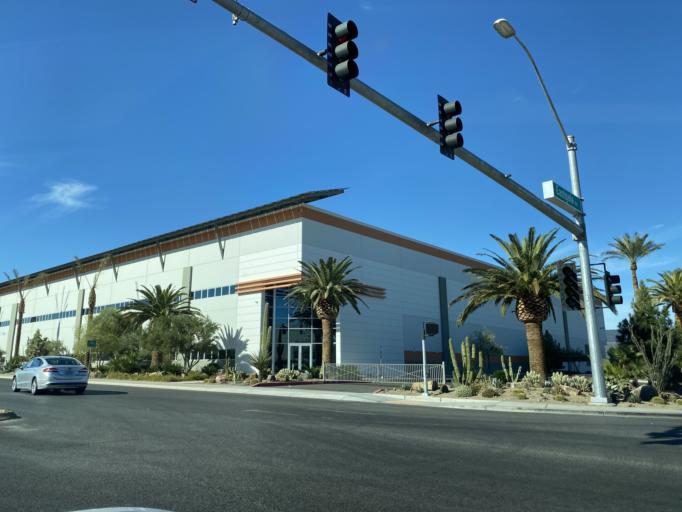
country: US
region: Nevada
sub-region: Clark County
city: Henderson
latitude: 36.0564
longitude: -115.0201
